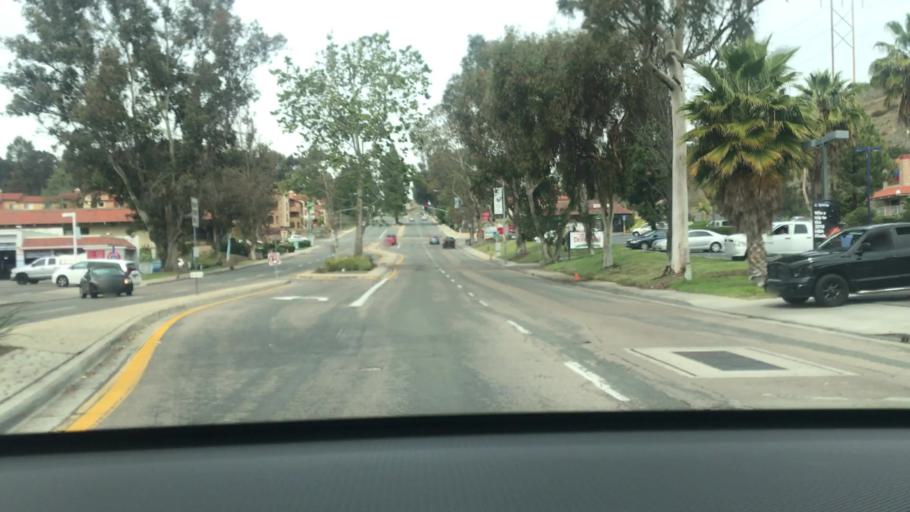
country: US
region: California
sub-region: San Diego County
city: Poway
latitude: 32.9502
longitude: -117.1072
